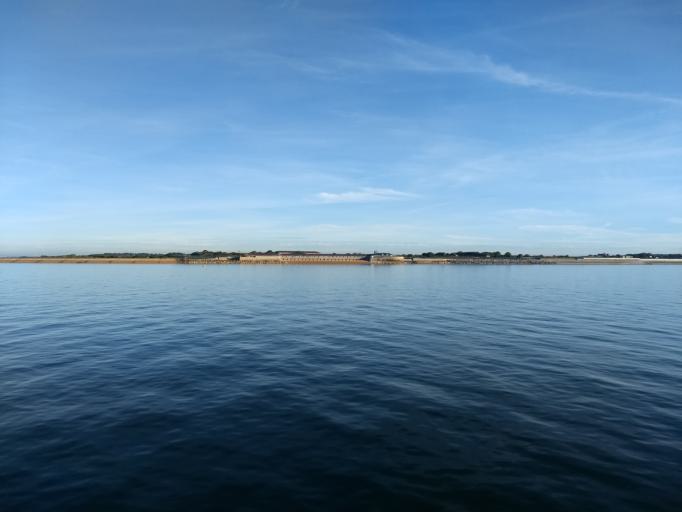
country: GB
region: England
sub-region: Hampshire
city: Gosport
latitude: 50.7713
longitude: -1.1276
